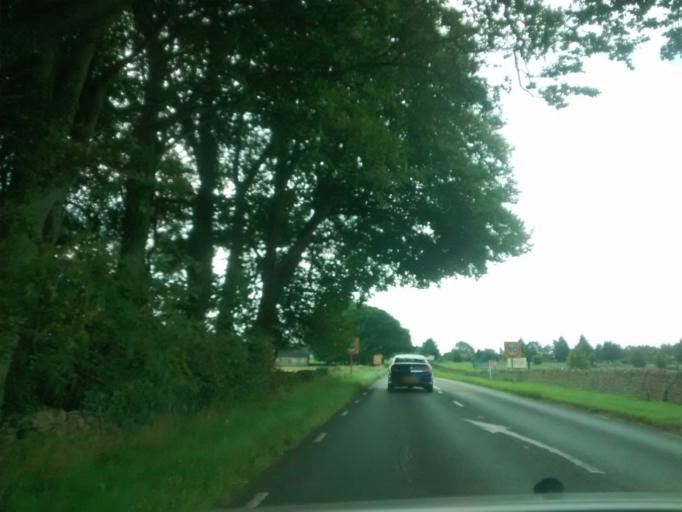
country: GB
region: England
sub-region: South Gloucestershire
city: Cold Ashton
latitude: 51.4219
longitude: -2.3989
